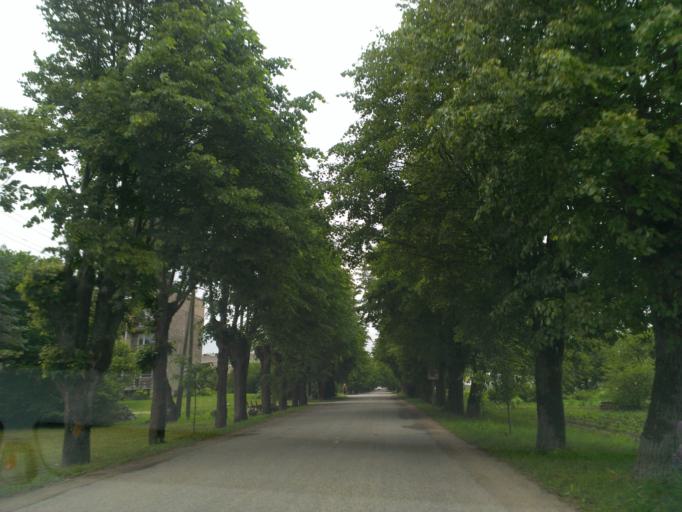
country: LV
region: Durbe
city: Liegi
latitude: 56.7327
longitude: 21.3921
